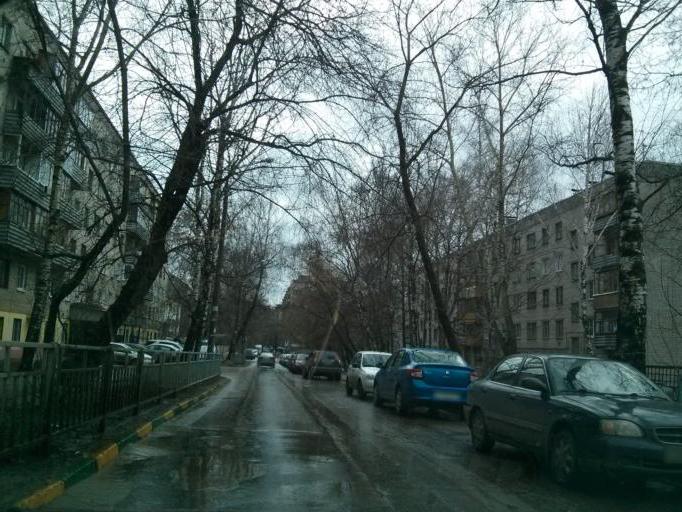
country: RU
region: Nizjnij Novgorod
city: Nizhniy Novgorod
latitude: 56.3189
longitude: 44.0469
